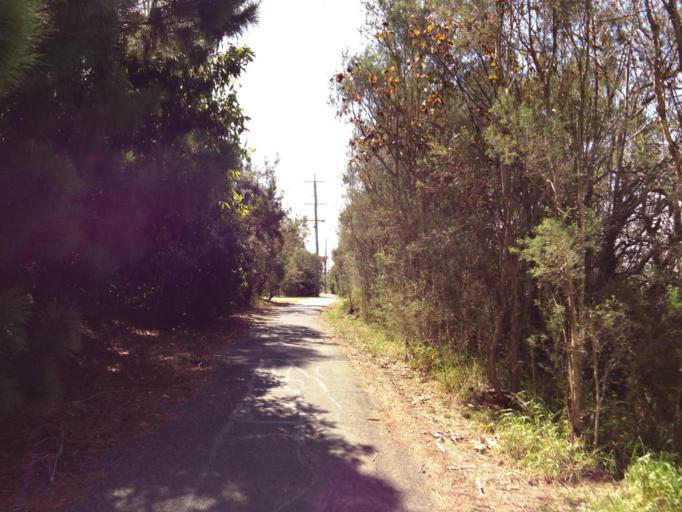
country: AU
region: Victoria
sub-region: Mornington Peninsula
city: Tyabb
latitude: -38.2421
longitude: 145.1904
